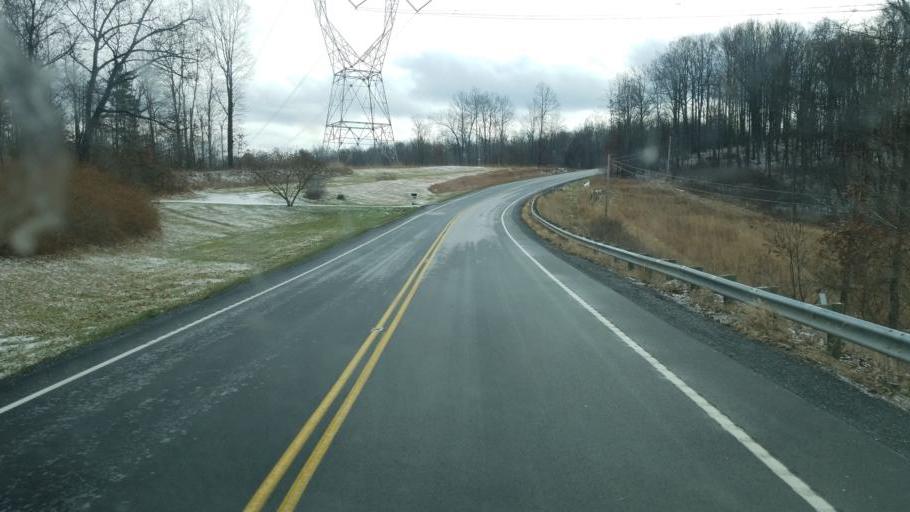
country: US
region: Ohio
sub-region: Muskingum County
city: Frazeysburg
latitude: 40.1156
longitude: -82.1840
